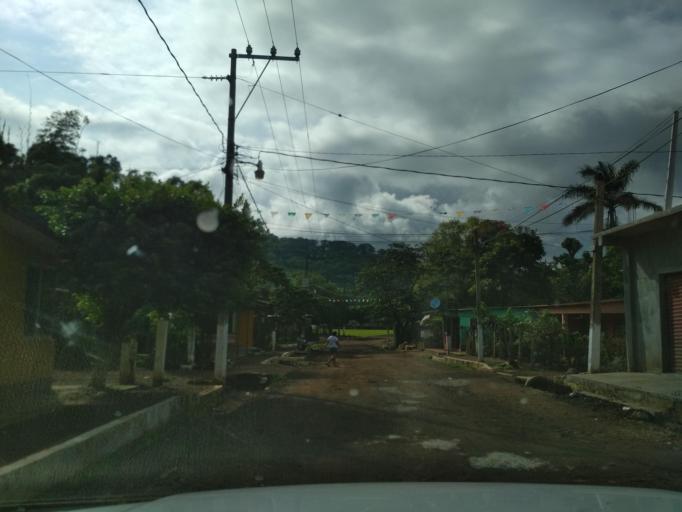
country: MX
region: Veracruz
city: Catemaco
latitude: 18.3726
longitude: -95.1185
